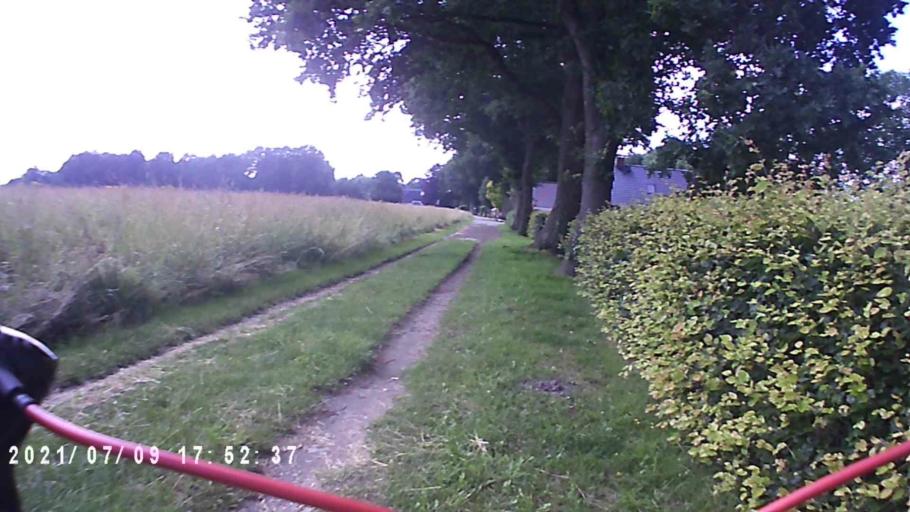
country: NL
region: Groningen
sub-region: Gemeente Vlagtwedde
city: Vlagtwedde
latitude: 53.0667
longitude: 7.0785
